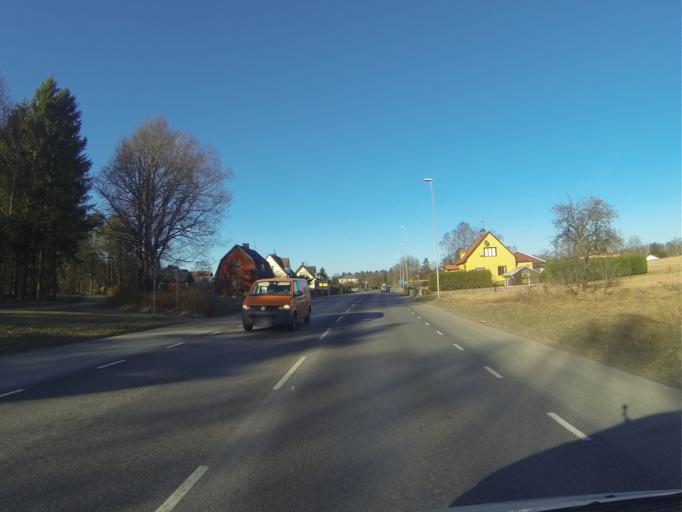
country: SE
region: Skane
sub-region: Hoors Kommun
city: Hoeoer
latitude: 55.9381
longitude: 13.5571
